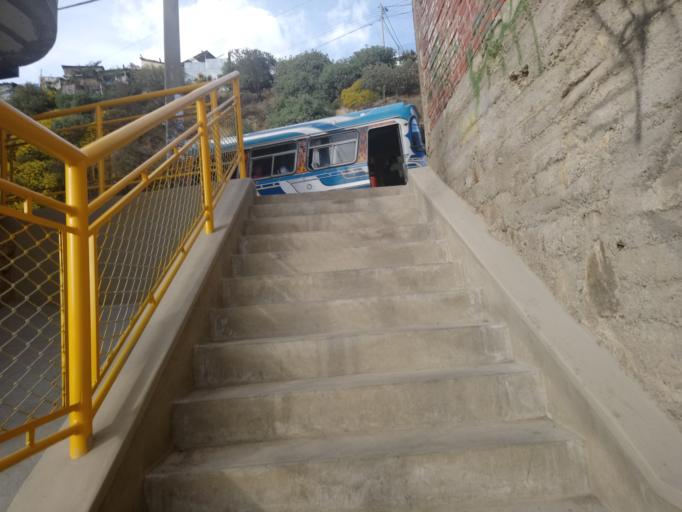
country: BO
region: La Paz
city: La Paz
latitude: -16.5018
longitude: -68.1060
